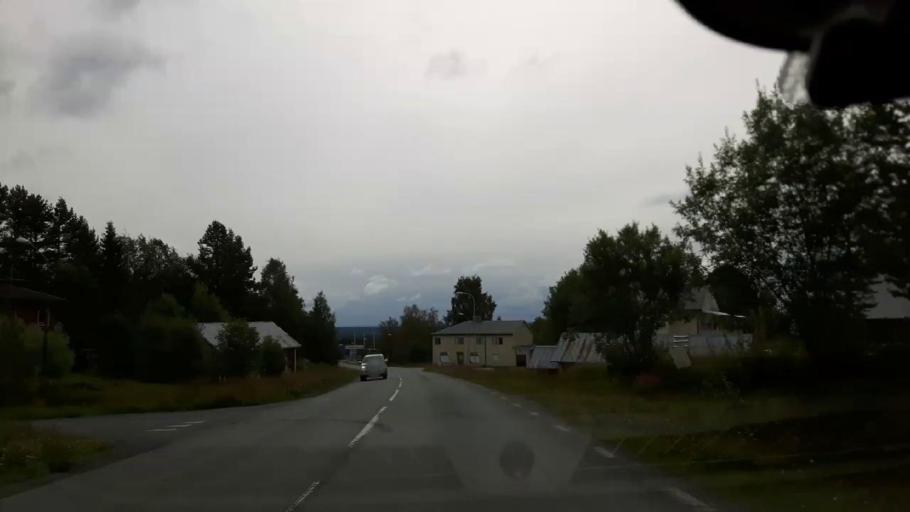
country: SE
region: Jaemtland
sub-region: Krokoms Kommun
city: Krokom
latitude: 63.4574
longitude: 14.1898
